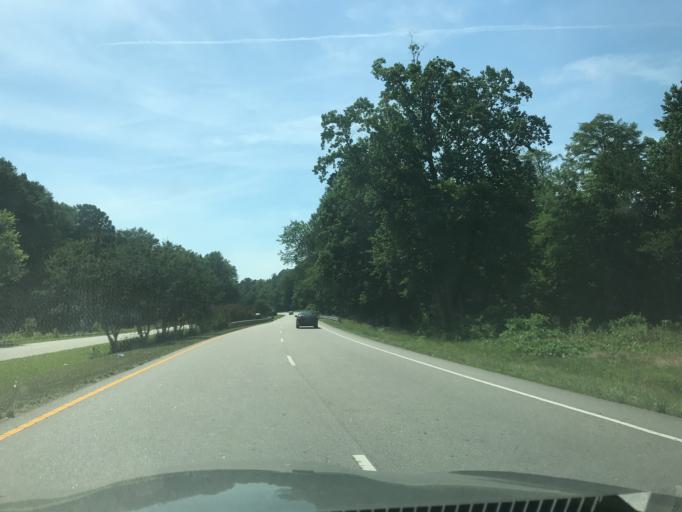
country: US
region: North Carolina
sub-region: Wake County
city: Wendell
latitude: 35.8023
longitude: -78.4063
